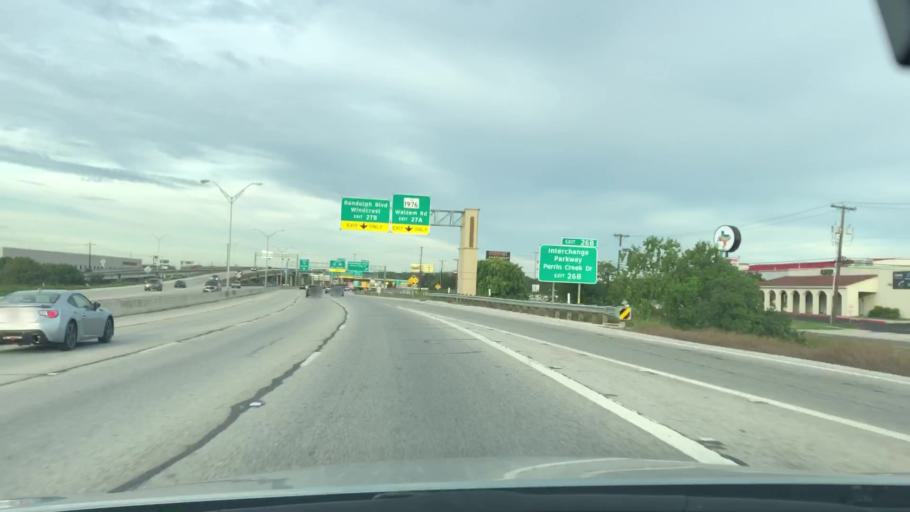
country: US
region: Texas
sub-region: Bexar County
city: Windcrest
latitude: 29.5170
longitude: -98.4012
